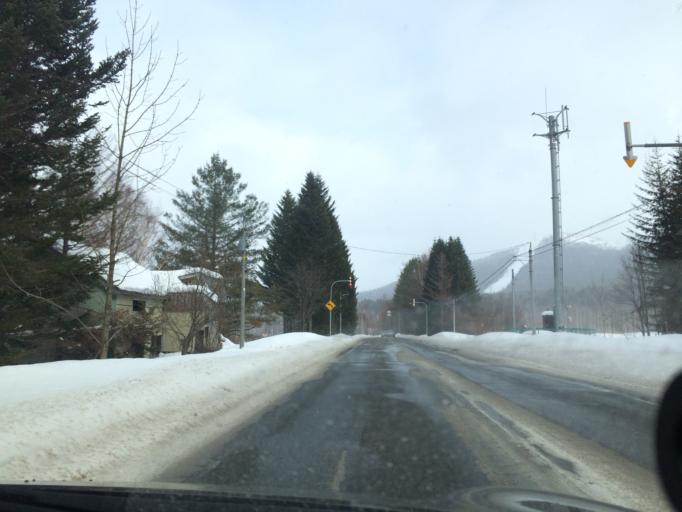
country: JP
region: Hokkaido
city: Shimo-furano
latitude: 43.0498
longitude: 142.6681
